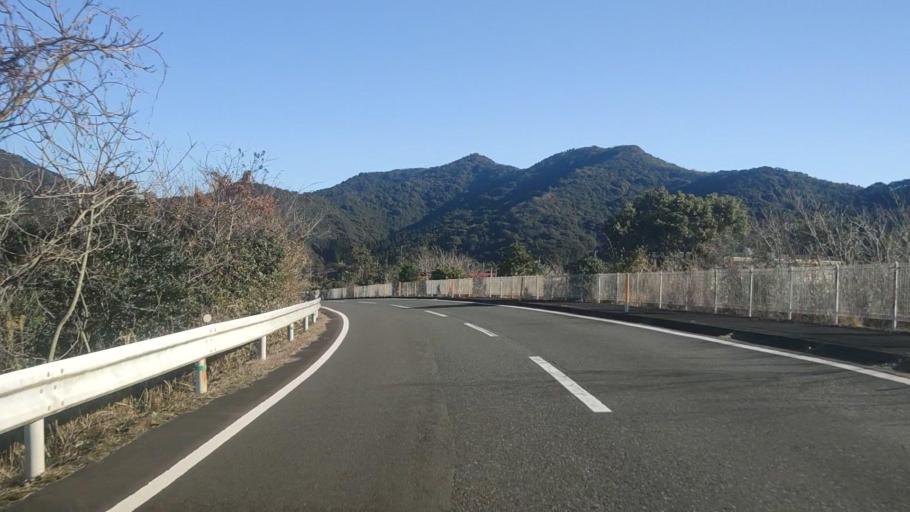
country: JP
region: Miyazaki
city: Nobeoka
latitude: 32.6775
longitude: 131.7831
